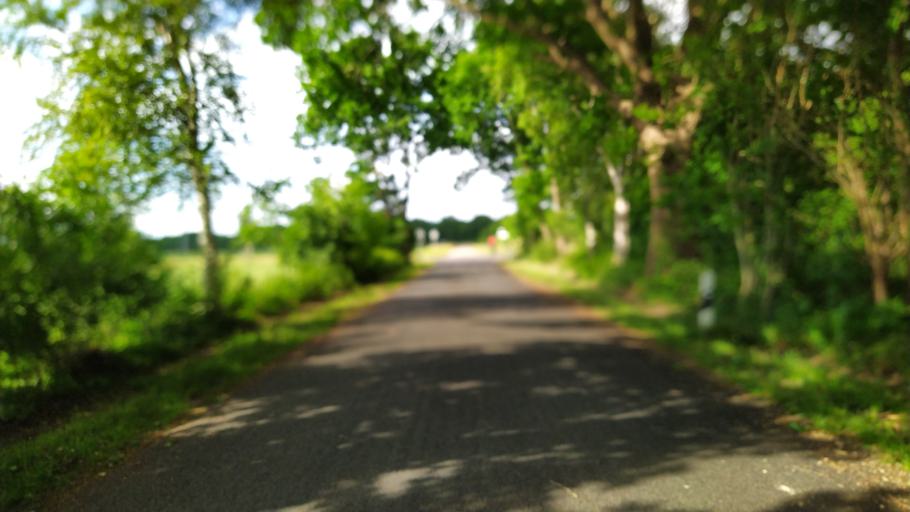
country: DE
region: Lower Saxony
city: Sandbostel
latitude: 53.4303
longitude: 9.1706
